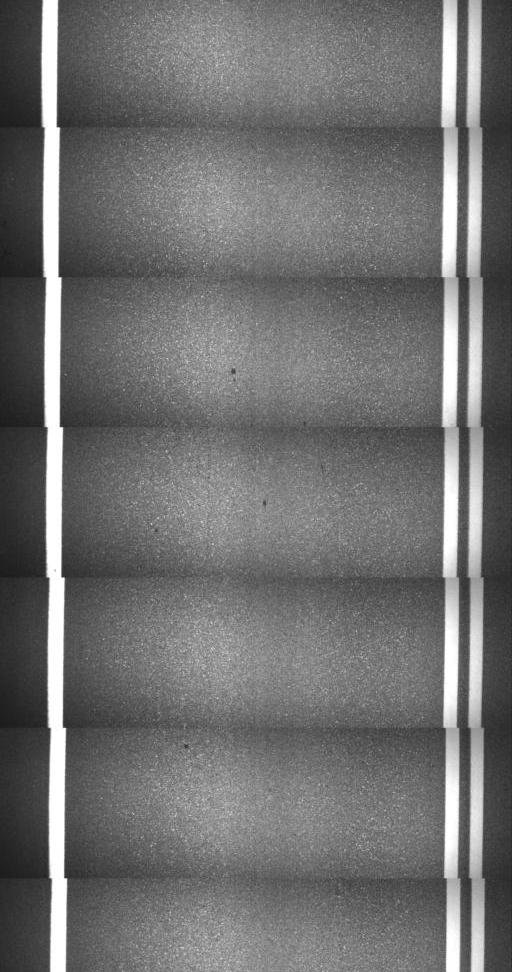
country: US
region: Vermont
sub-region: Windham County
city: Dover
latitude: 43.0674
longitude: -72.8623
